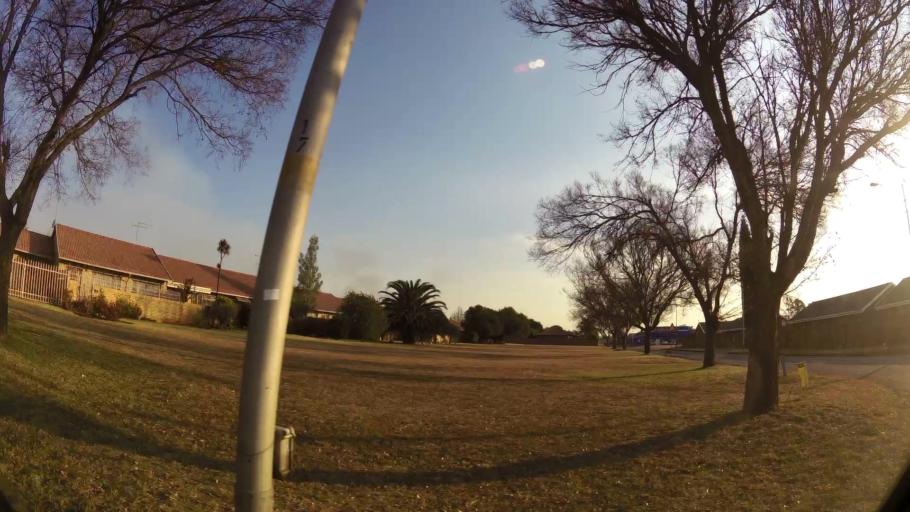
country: ZA
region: Gauteng
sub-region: Ekurhuleni Metropolitan Municipality
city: Springs
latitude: -26.2540
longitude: 28.4043
